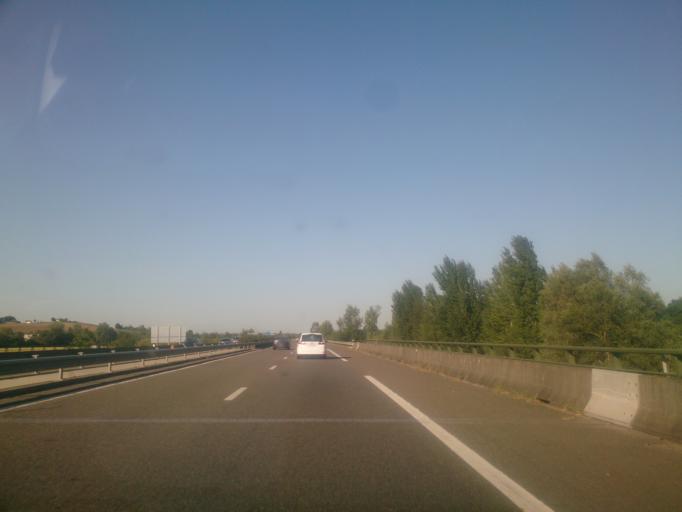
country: FR
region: Midi-Pyrenees
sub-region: Departement du Tarn-et-Garonne
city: Caussade
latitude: 44.1457
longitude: 1.5056
